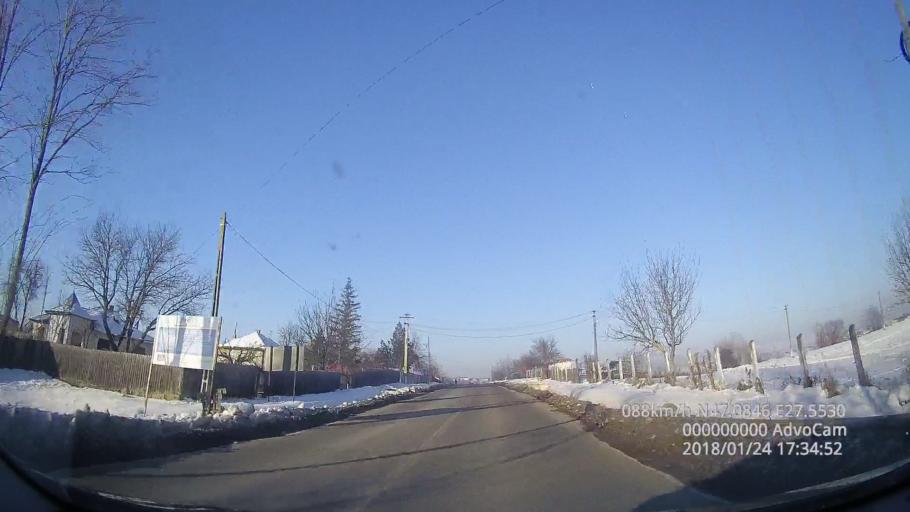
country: RO
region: Iasi
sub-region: Comuna Ciurea
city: Dumbrava
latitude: 47.0853
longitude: 27.5533
